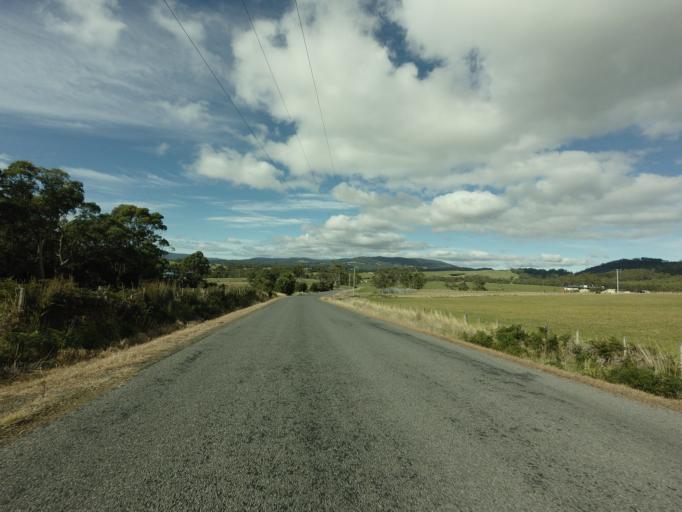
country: AU
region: Tasmania
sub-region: Clarence
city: Sandford
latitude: -43.0399
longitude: 147.7422
